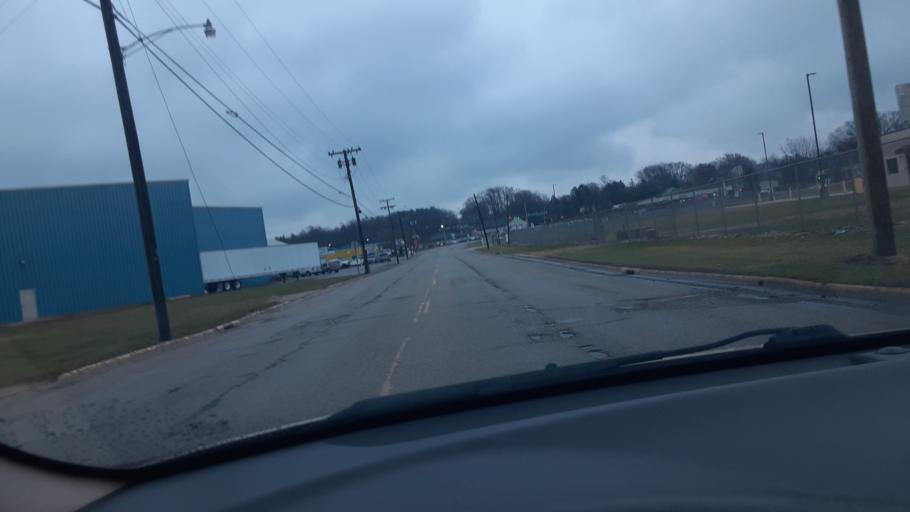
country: US
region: Illinois
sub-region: Winnebago County
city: Loves Park
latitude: 42.3107
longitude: -89.0447
